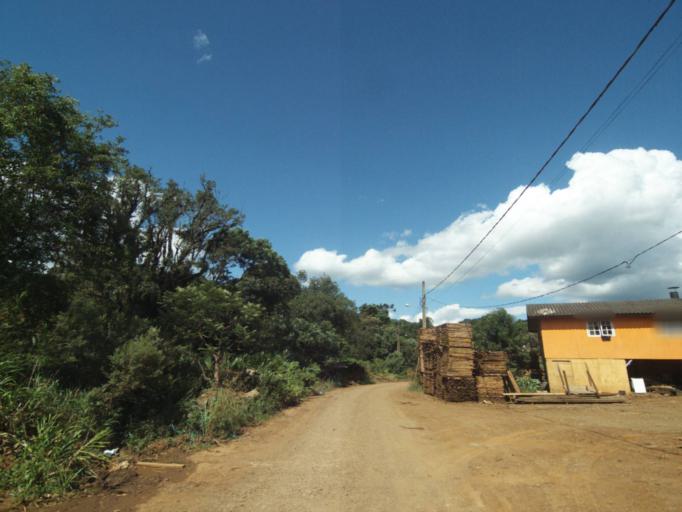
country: BR
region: Parana
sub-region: Uniao Da Vitoria
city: Uniao da Vitoria
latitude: -26.1499
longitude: -51.5401
